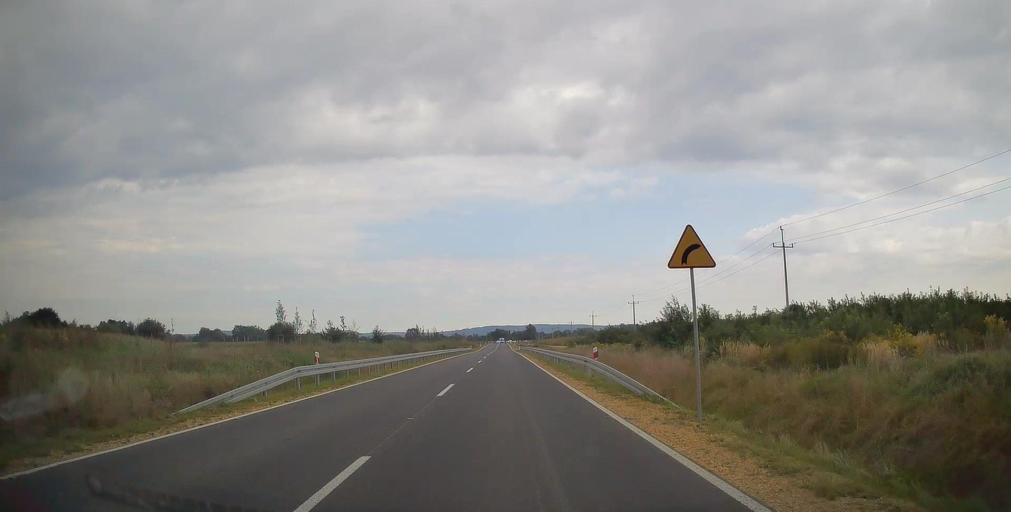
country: PL
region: Lesser Poland Voivodeship
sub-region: Powiat oswiecimski
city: Zator
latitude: 50.0146
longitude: 19.4268
